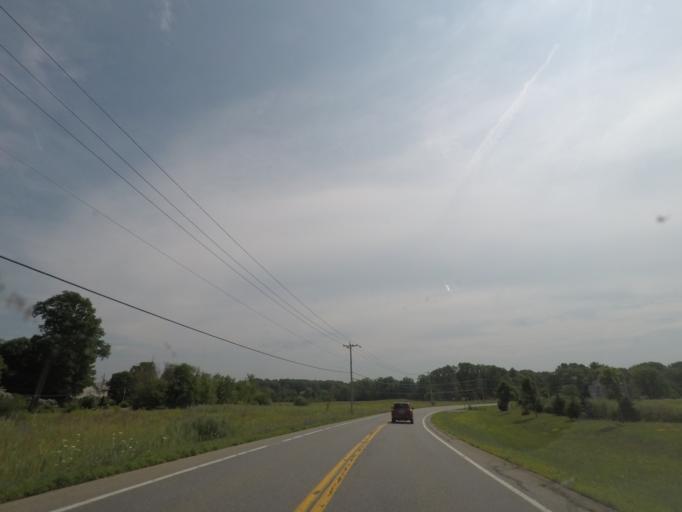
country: US
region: New York
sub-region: Saratoga County
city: Country Knolls
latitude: 42.8944
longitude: -73.7500
